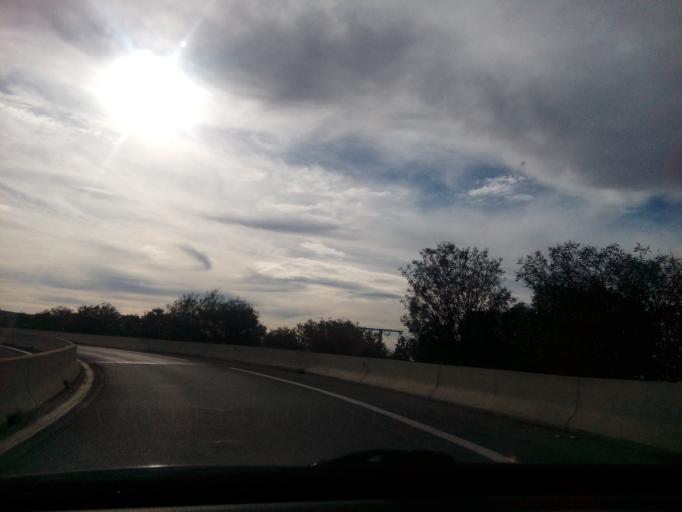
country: DZ
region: Sidi Bel Abbes
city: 'Ain el Berd
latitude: 35.3819
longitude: -0.5020
